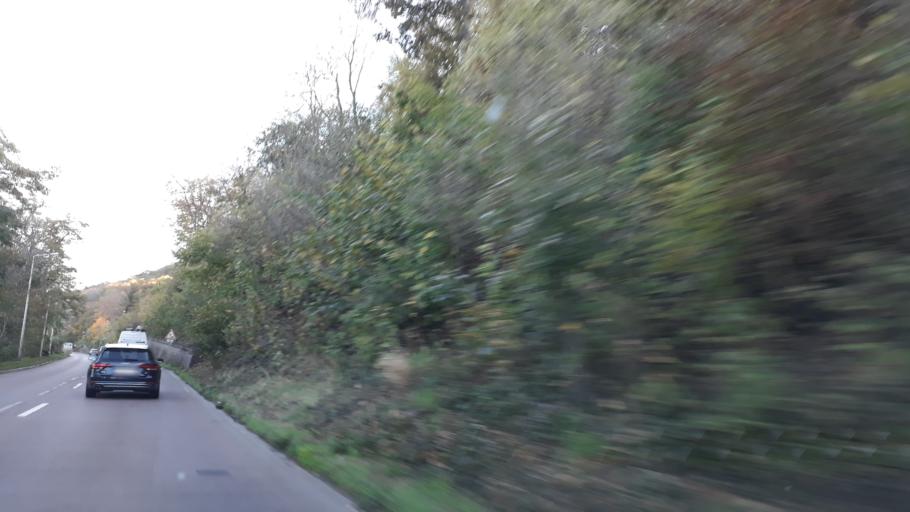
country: DE
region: Saxony
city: Coswig
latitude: 51.0904
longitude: 13.6094
